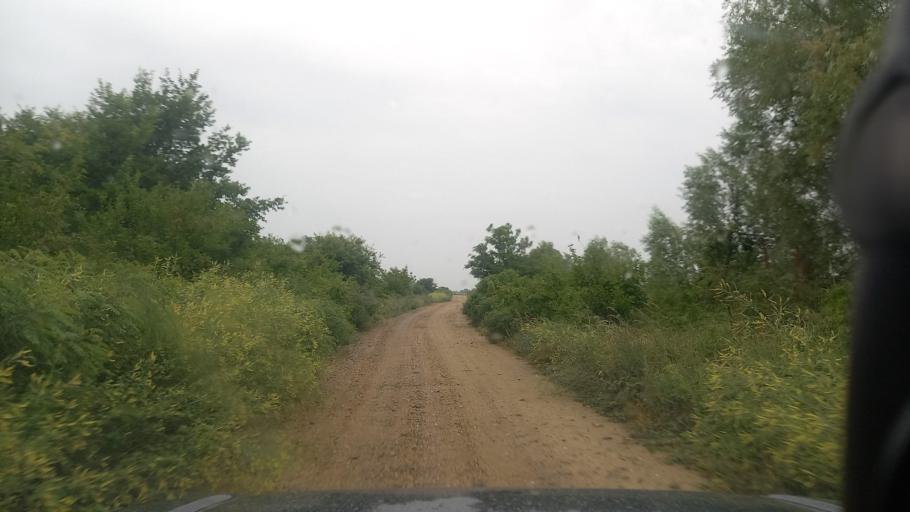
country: RU
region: Krasnodarskiy
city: Ryazanskaya
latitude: 45.0204
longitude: 39.4941
